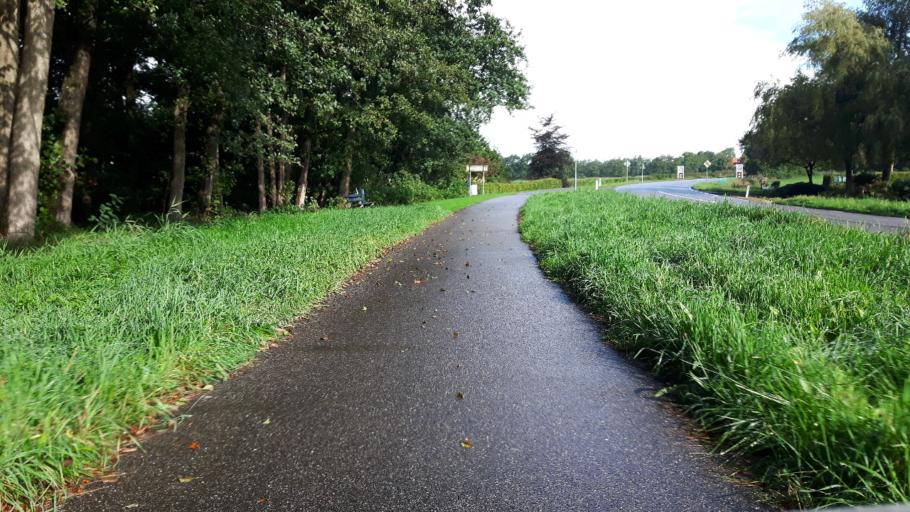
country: NL
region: Friesland
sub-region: Gemeente Smallingerland
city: Drachten
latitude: 53.0744
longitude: 6.0979
